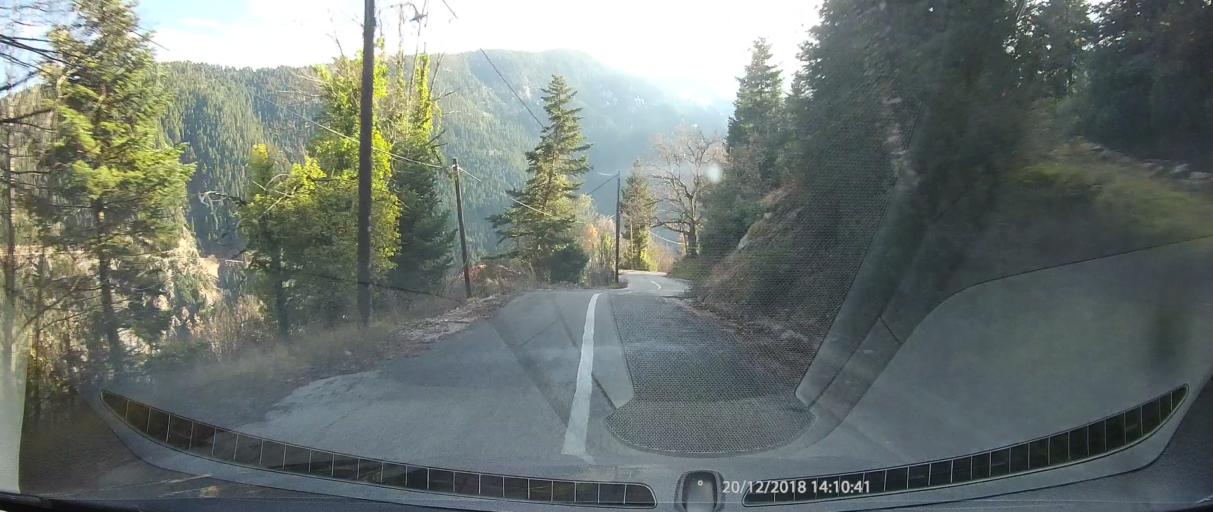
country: GR
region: West Greece
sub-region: Nomos Aitolias kai Akarnanias
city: Thermo
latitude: 38.7440
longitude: 21.6507
